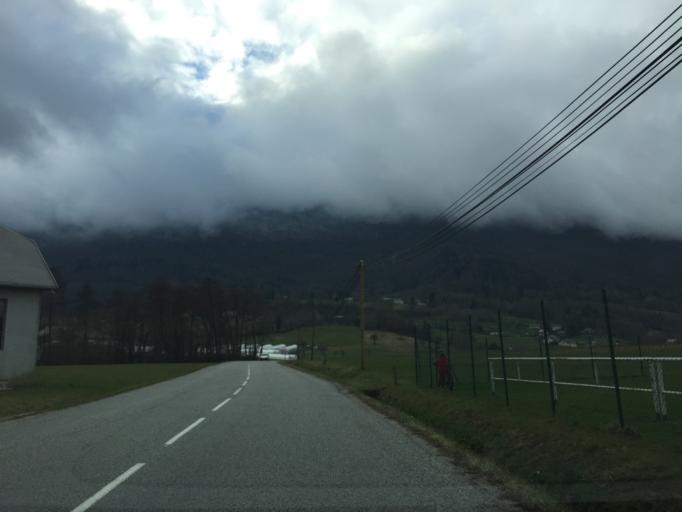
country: FR
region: Rhone-Alpes
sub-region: Departement de la Savoie
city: Vimines
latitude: 45.5382
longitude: 5.8583
